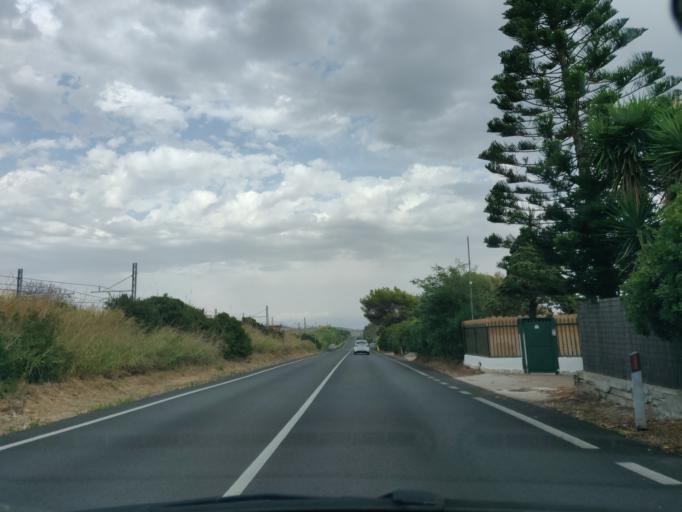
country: IT
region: Latium
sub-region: Citta metropolitana di Roma Capitale
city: Santa Marinella
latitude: 42.0409
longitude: 11.9101
